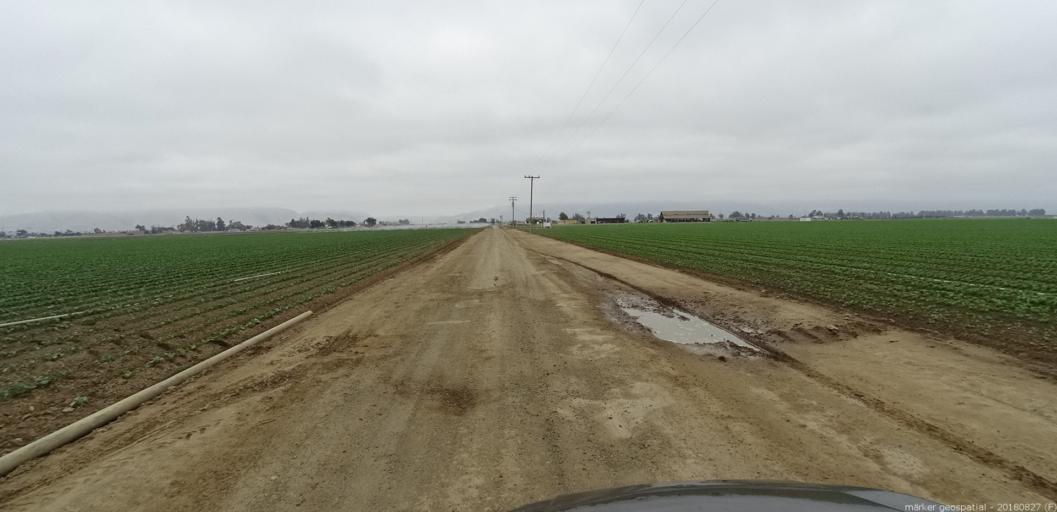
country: US
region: California
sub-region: Monterey County
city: Greenfield
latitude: 36.3411
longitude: -121.2387
